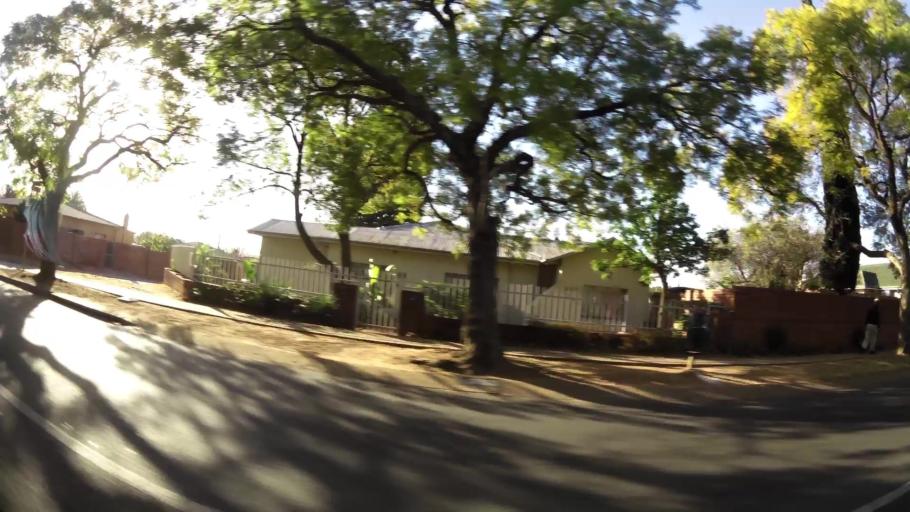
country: ZA
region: Gauteng
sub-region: City of Tshwane Metropolitan Municipality
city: Pretoria
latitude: -25.7221
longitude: 28.2246
